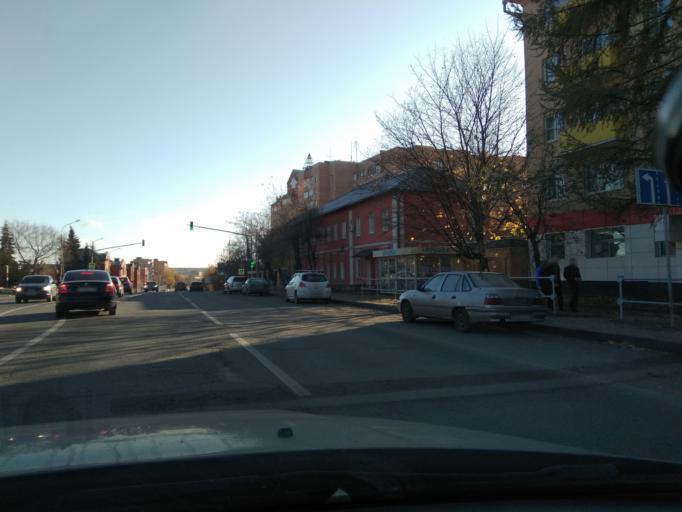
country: RU
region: Moskovskaya
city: Istra
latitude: 55.9139
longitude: 36.8607
